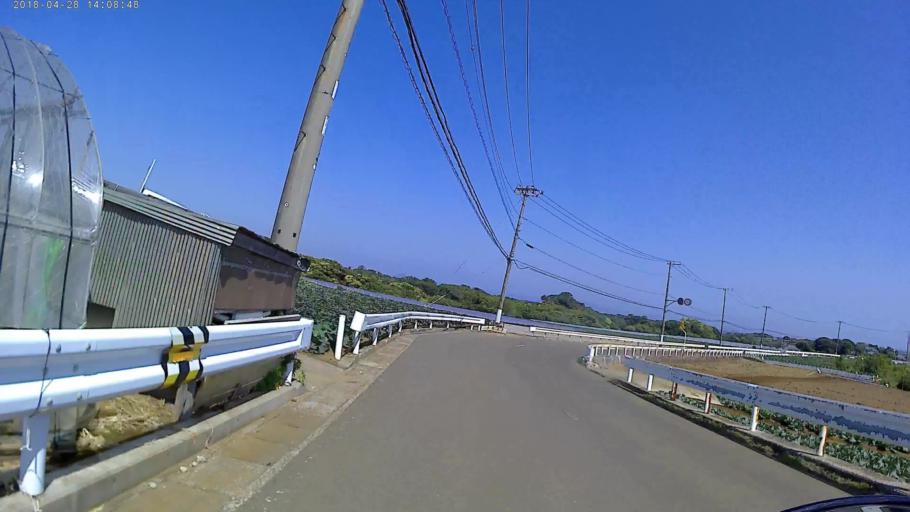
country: JP
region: Kanagawa
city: Miura
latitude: 35.1495
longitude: 139.6500
